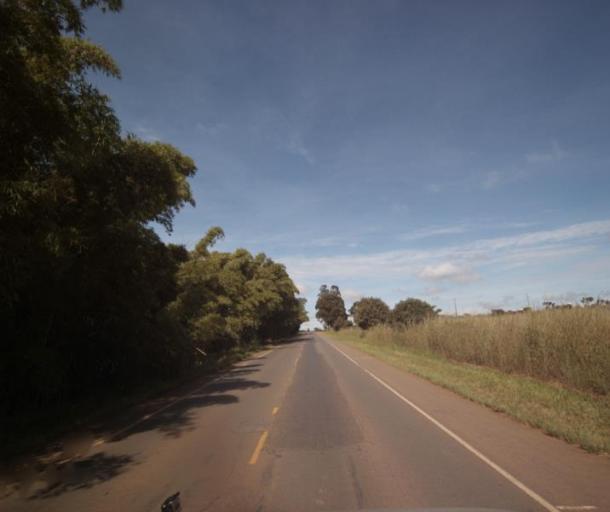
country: BR
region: Goias
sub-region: Anapolis
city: Anapolis
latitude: -16.2190
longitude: -48.9215
